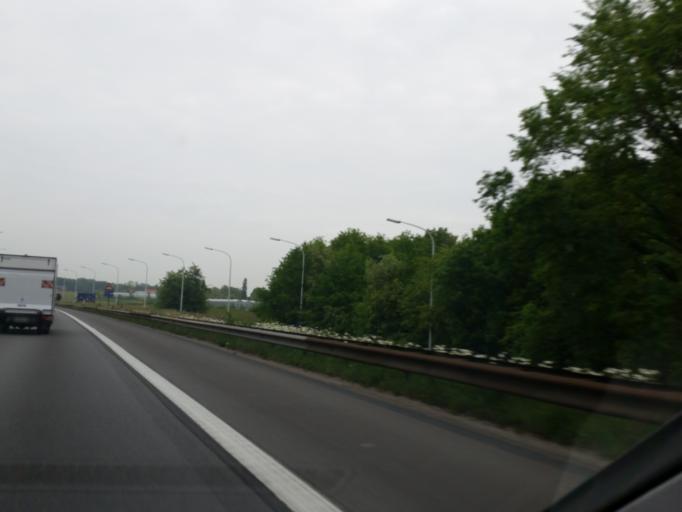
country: BE
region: Flanders
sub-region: Provincie Antwerpen
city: Rumst
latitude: 51.0855
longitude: 4.4435
